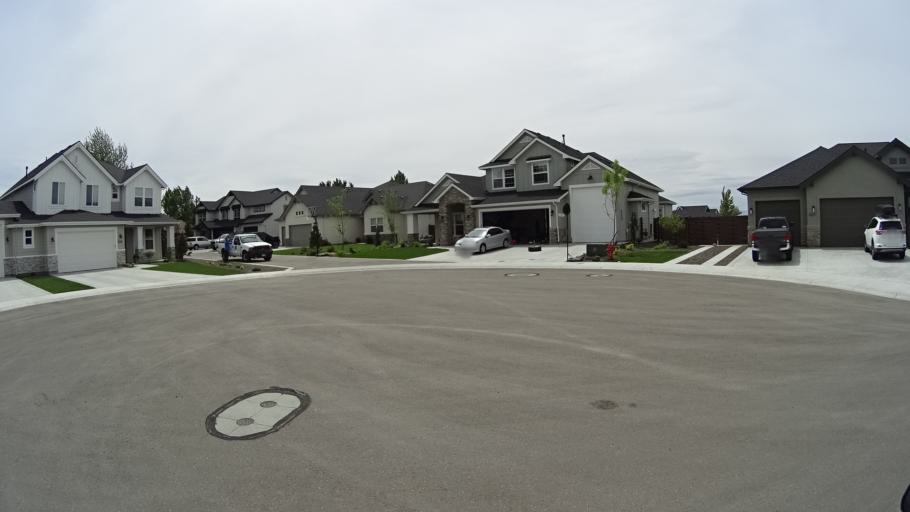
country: US
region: Idaho
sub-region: Ada County
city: Meridian
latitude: 43.5563
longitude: -116.3401
